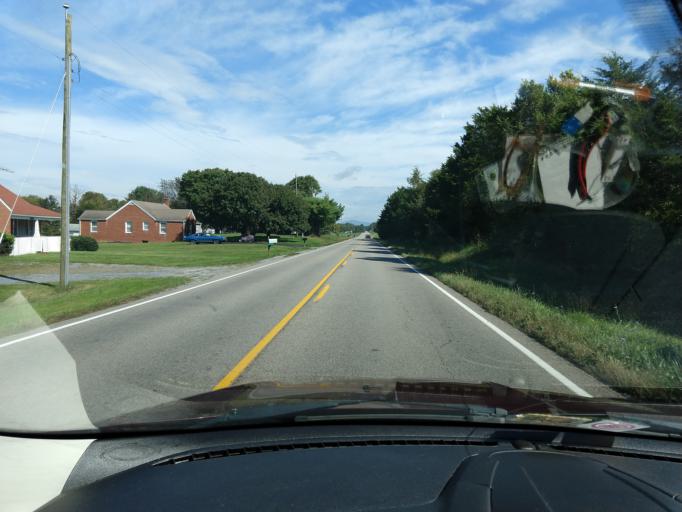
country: US
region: Virginia
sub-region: Augusta County
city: Crimora
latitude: 38.1916
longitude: -78.8393
